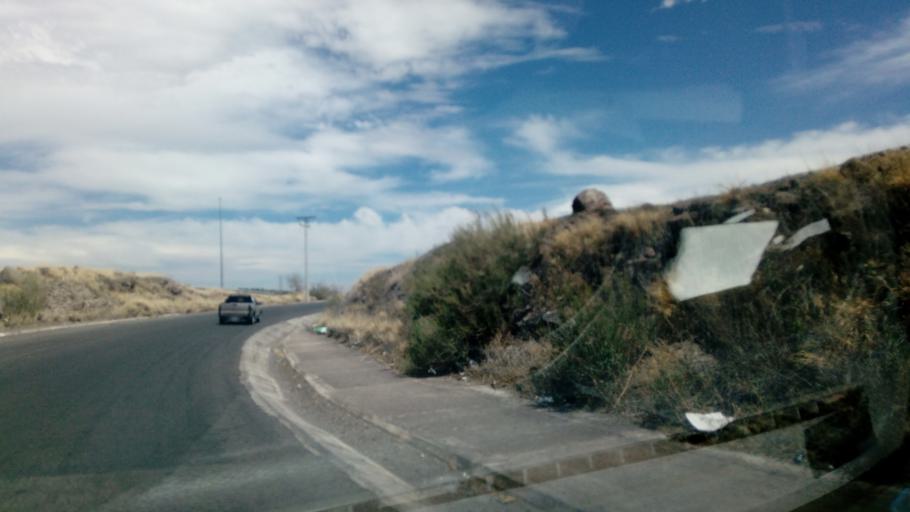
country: MX
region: Durango
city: Victoria de Durango
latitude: 24.0766
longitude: -104.6224
